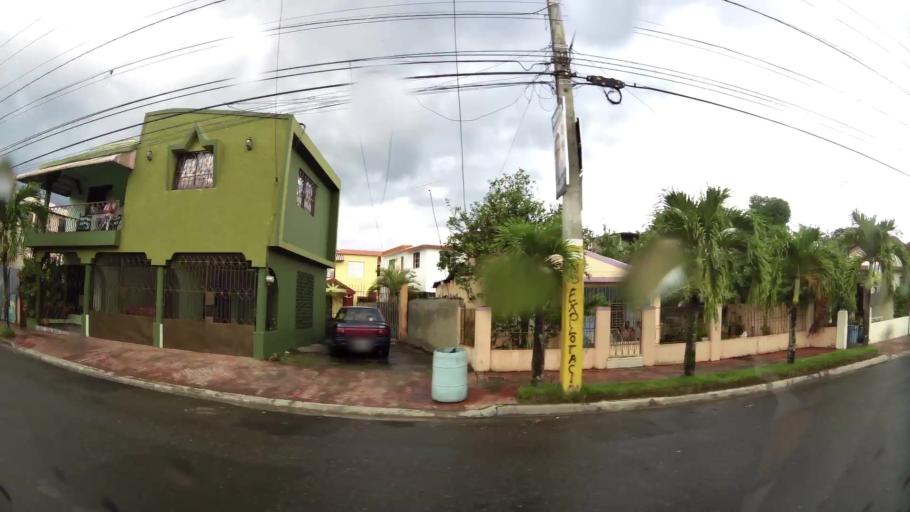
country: DO
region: Monsenor Nouel
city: Bonao
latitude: 18.9396
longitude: -70.3972
